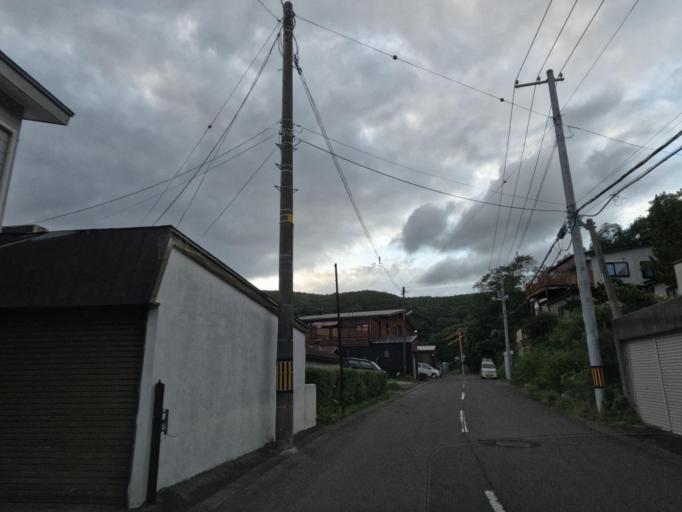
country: JP
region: Hokkaido
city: Muroran
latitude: 42.3633
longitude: 140.9666
